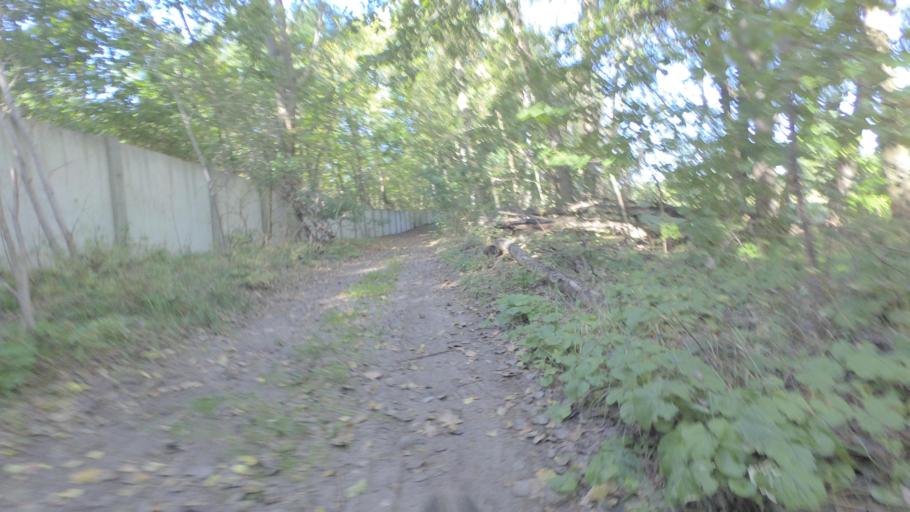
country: DE
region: Brandenburg
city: Sperenberg
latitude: 52.1466
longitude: 13.3482
